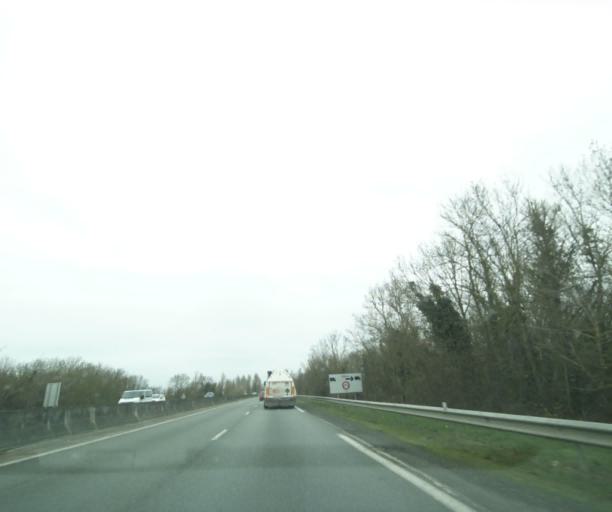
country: FR
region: Poitou-Charentes
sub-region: Departement de la Charente-Maritime
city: Angoulins
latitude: 46.1197
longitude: -1.1085
